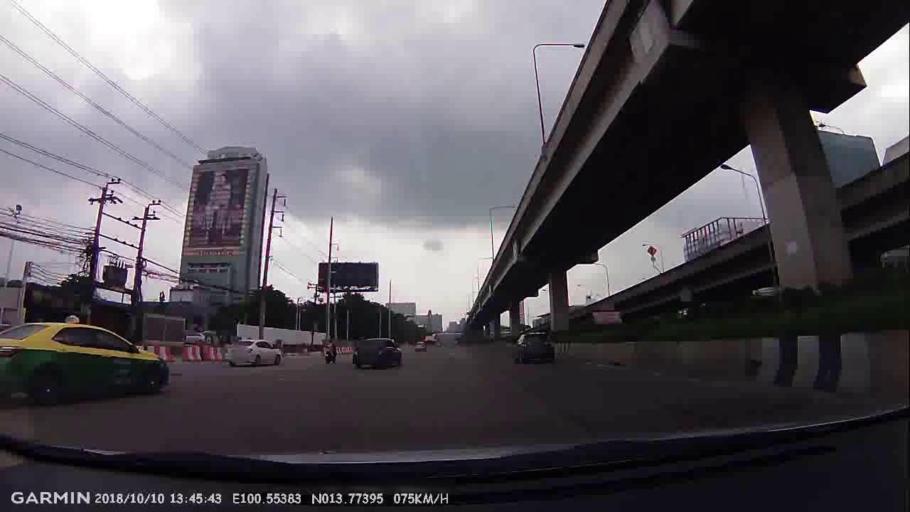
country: TH
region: Bangkok
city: Din Daeng
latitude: 13.7739
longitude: 100.5538
